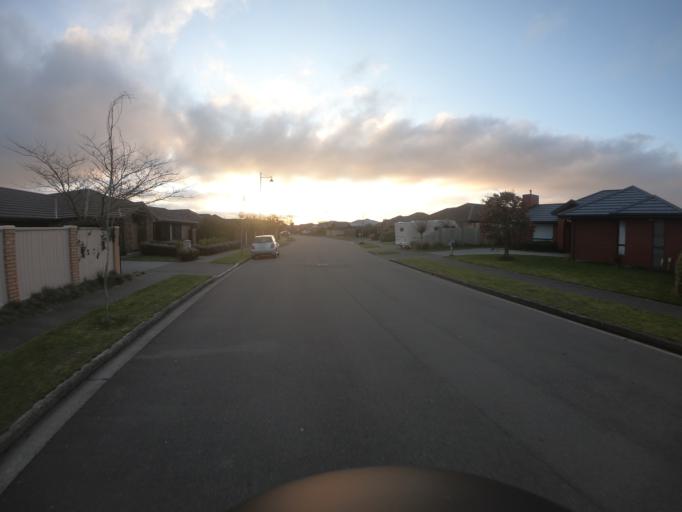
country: NZ
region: Canterbury
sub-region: Selwyn District
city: Prebbleton
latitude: -43.5670
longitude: 172.5622
